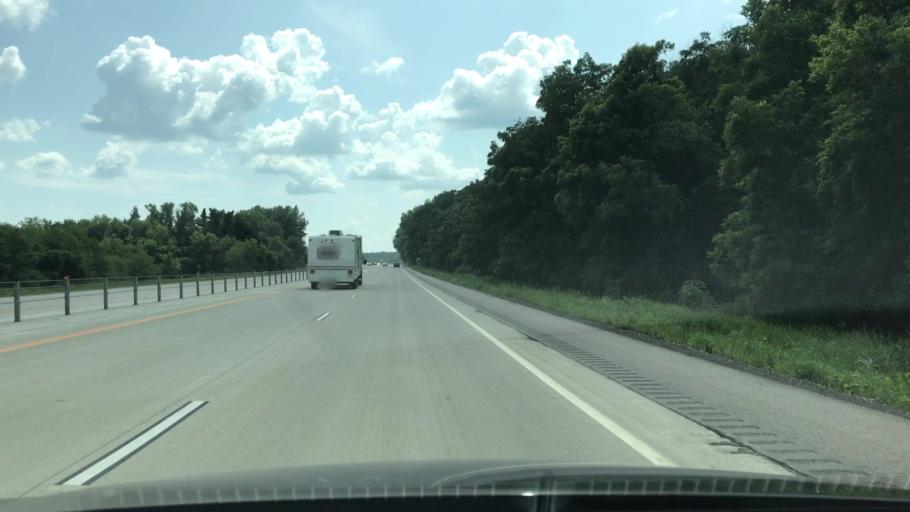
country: US
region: Minnesota
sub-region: Nicollet County
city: Saint Peter
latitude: 44.2809
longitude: -94.0096
